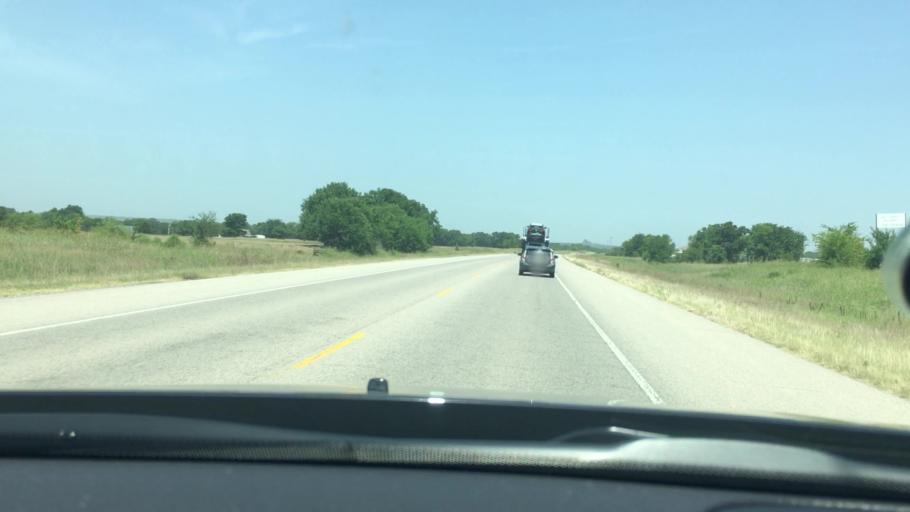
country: US
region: Oklahoma
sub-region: Pontotoc County
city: Ada
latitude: 34.7055
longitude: -96.6093
